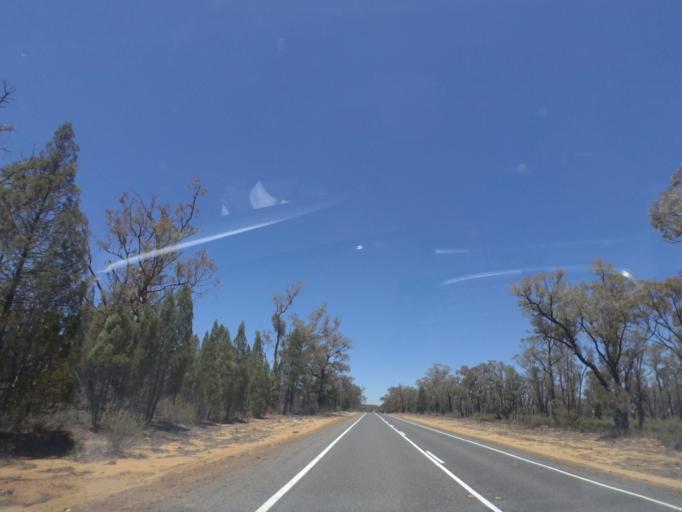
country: AU
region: New South Wales
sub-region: Narrabri
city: Narrabri
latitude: -30.7145
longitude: 149.5284
